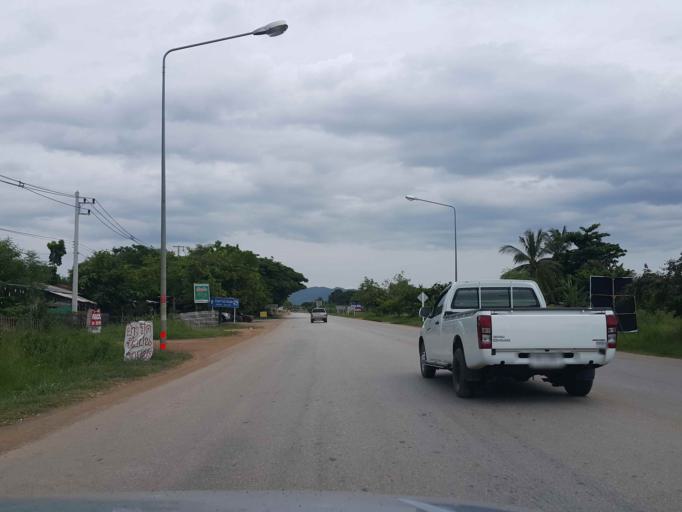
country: TH
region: Lampang
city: Lampang
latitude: 18.2620
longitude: 99.4702
